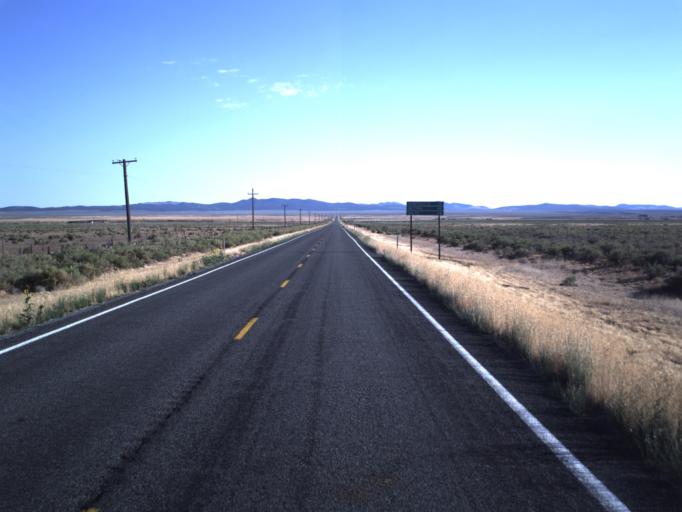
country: US
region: Utah
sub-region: Iron County
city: Enoch
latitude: 37.8644
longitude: -113.0316
